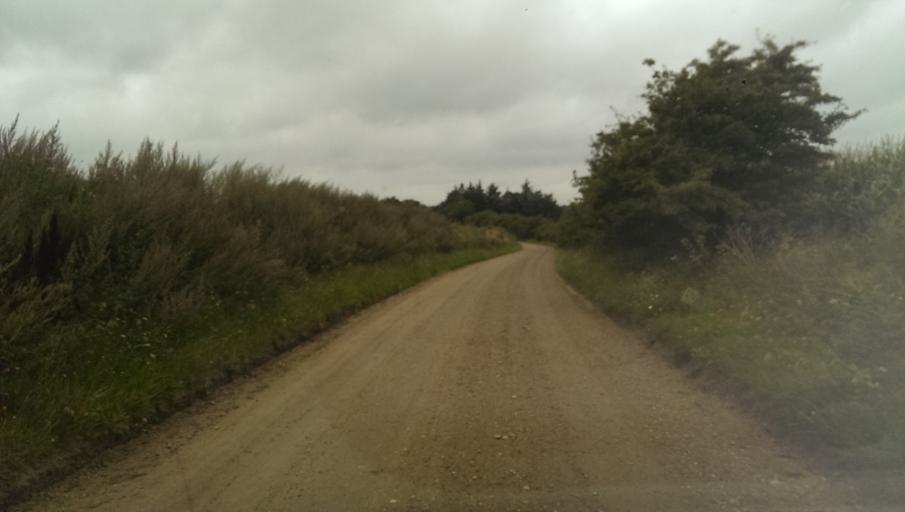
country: DK
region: South Denmark
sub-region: Esbjerg Kommune
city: Tjaereborg
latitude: 55.4796
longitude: 8.6007
